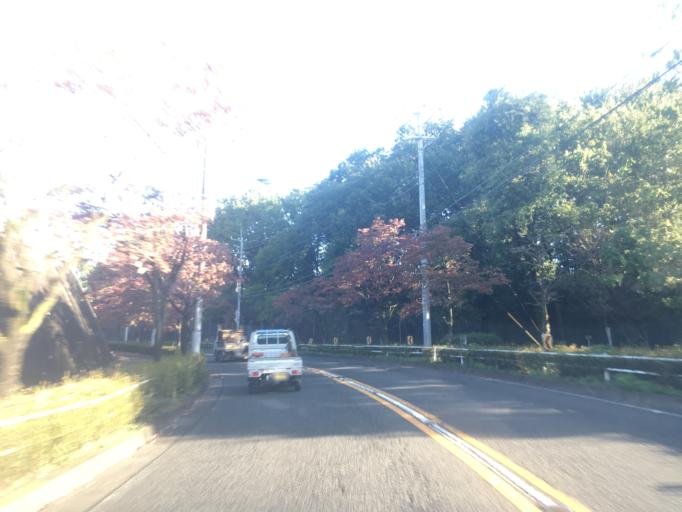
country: JP
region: Tokyo
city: Hino
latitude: 35.6828
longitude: 139.3586
